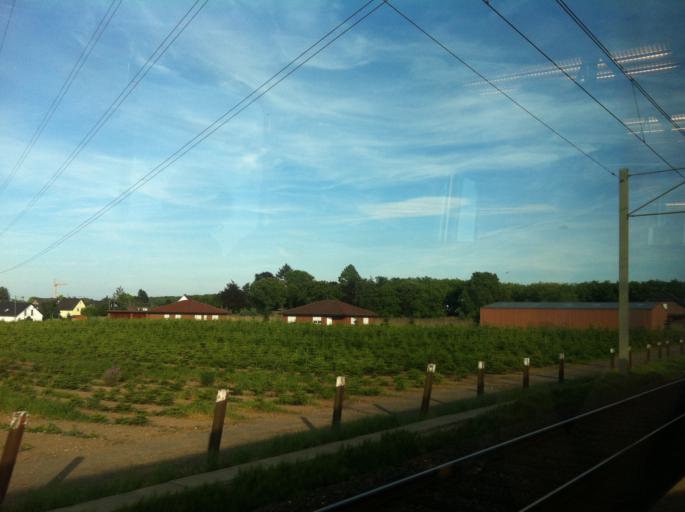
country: DE
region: North Rhine-Westphalia
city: Niederkassel
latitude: 50.7970
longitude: 7.0176
